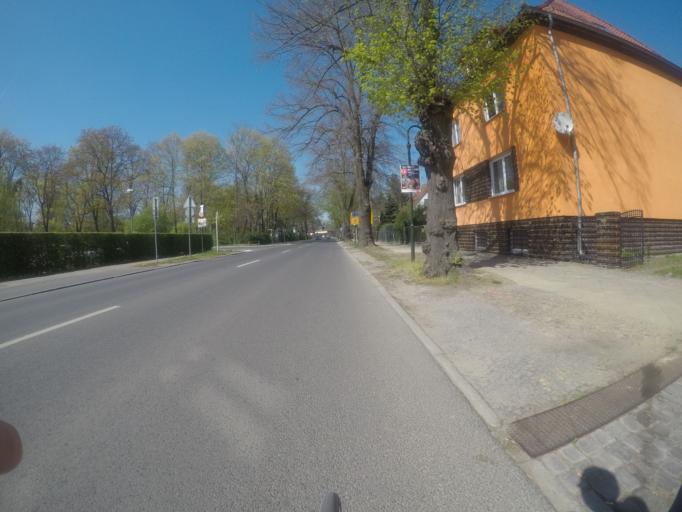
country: DE
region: Brandenburg
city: Bernau bei Berlin
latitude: 52.6805
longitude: 13.5921
